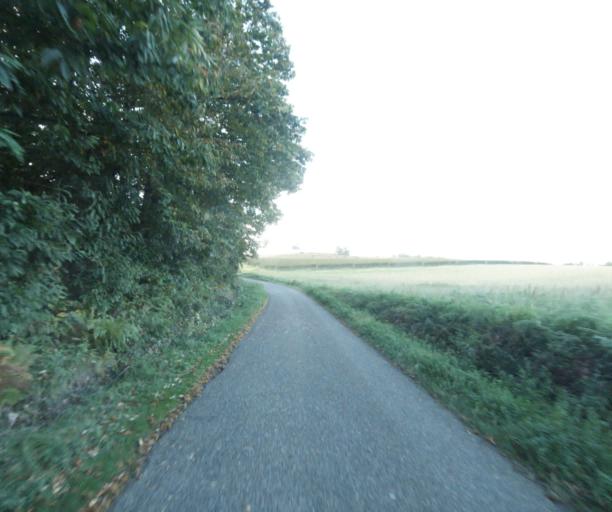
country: FR
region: Midi-Pyrenees
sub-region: Departement du Gers
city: Cazaubon
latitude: 43.8395
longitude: -0.0883
